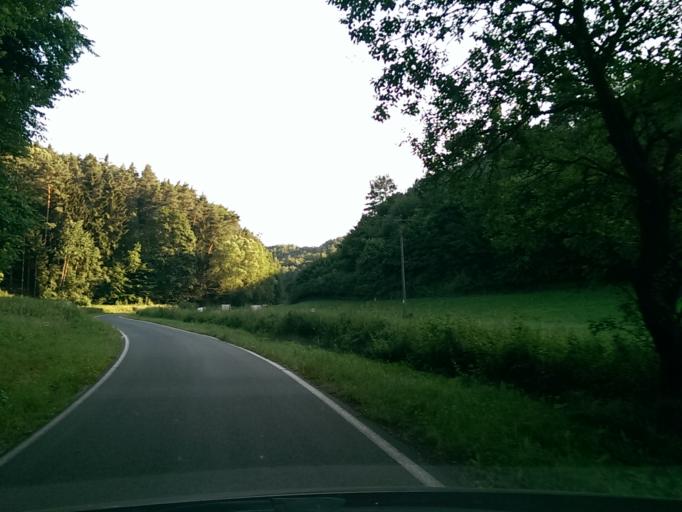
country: CZ
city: Duba
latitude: 50.4892
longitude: 14.5119
